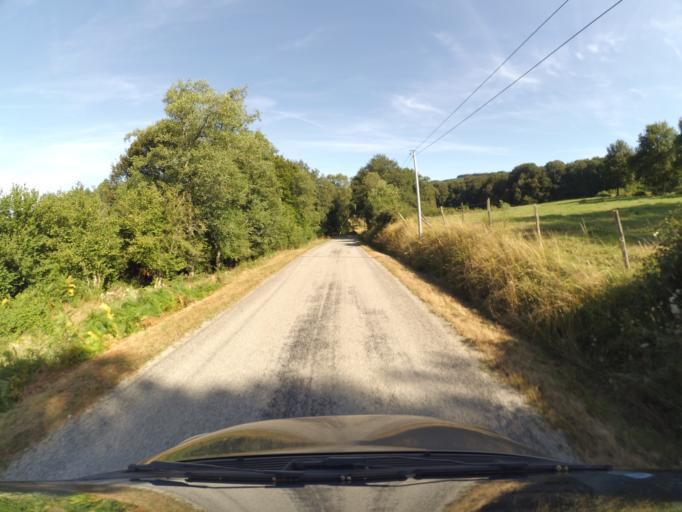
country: FR
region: Limousin
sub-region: Departement de la Correze
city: Bugeat
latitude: 45.6851
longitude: 1.8966
